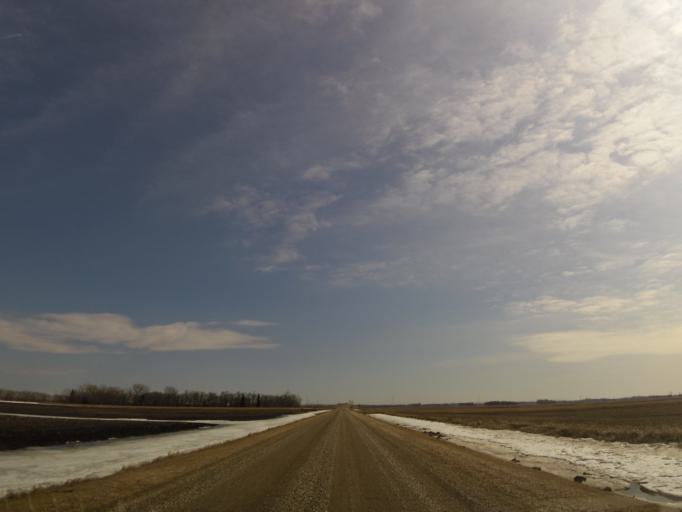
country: US
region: North Dakota
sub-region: Walsh County
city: Grafton
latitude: 48.3243
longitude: -97.1996
